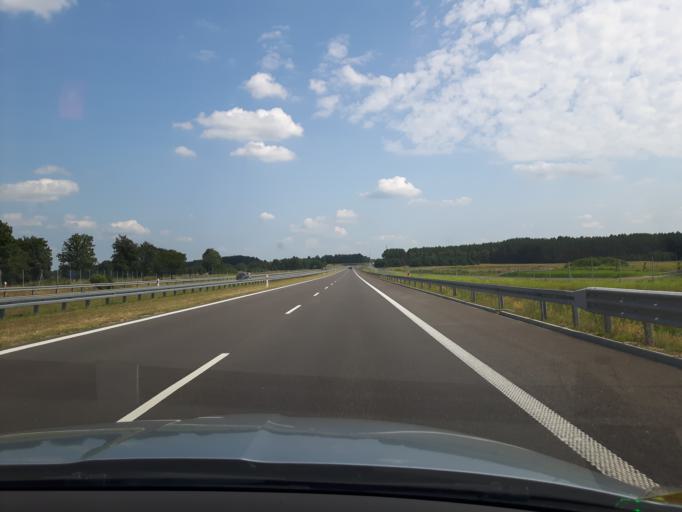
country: PL
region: Warmian-Masurian Voivodeship
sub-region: Powiat olsztynski
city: Olsztynek
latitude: 53.5881
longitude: 20.2212
